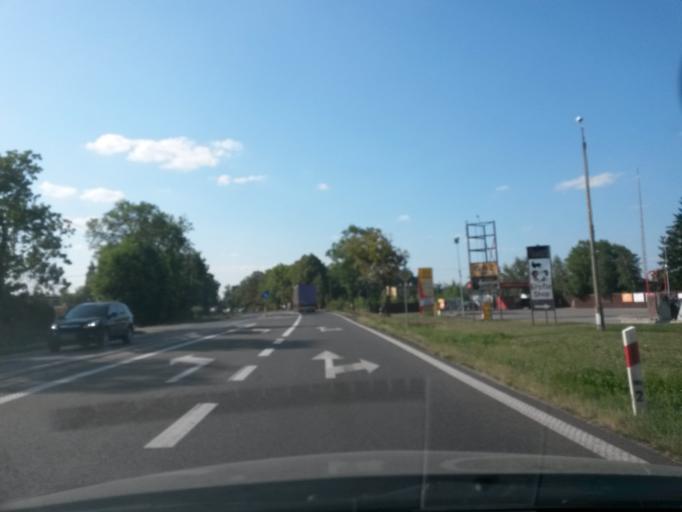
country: PL
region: Masovian Voivodeship
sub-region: Powiat sierpecki
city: Sierpc
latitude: 52.8594
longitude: 19.6797
